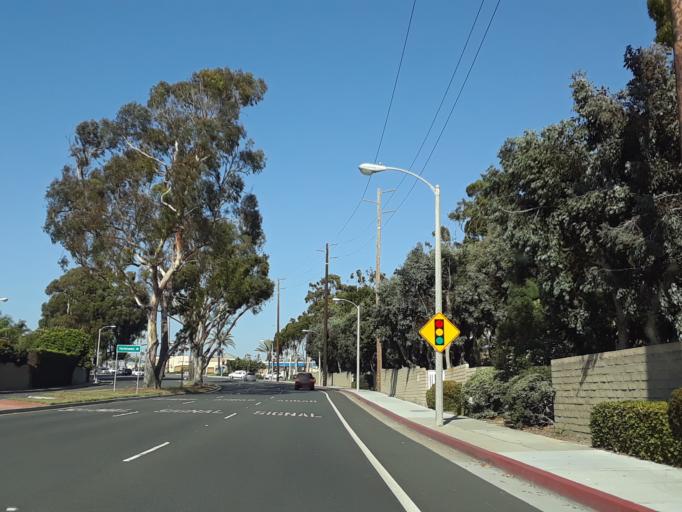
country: US
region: California
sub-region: Orange County
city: Huntington Beach
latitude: 33.6779
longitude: -118.0074
